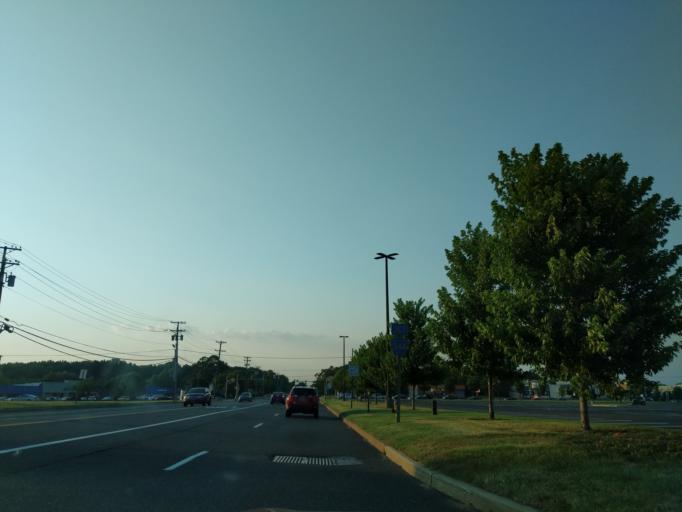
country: US
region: New Jersey
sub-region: Camden County
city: Glendora
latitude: 39.8316
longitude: -75.1008
